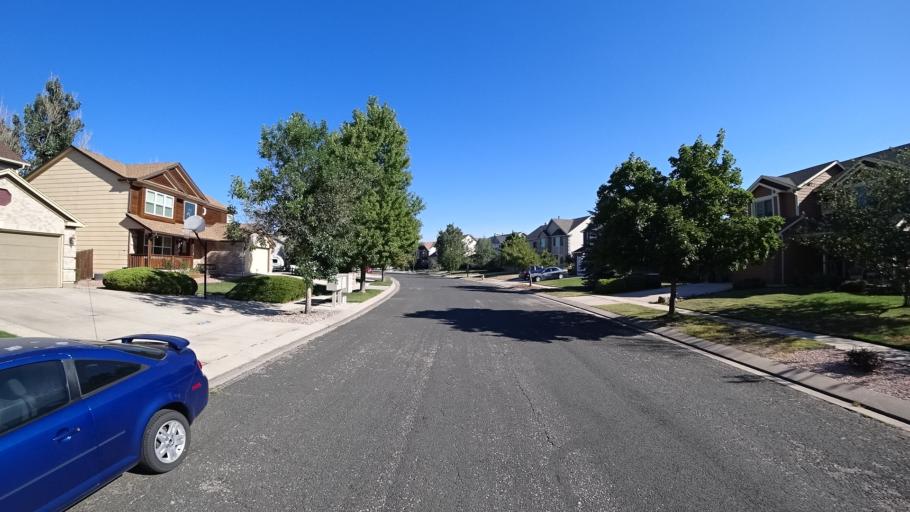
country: US
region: Colorado
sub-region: El Paso County
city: Black Forest
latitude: 38.9594
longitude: -104.7572
